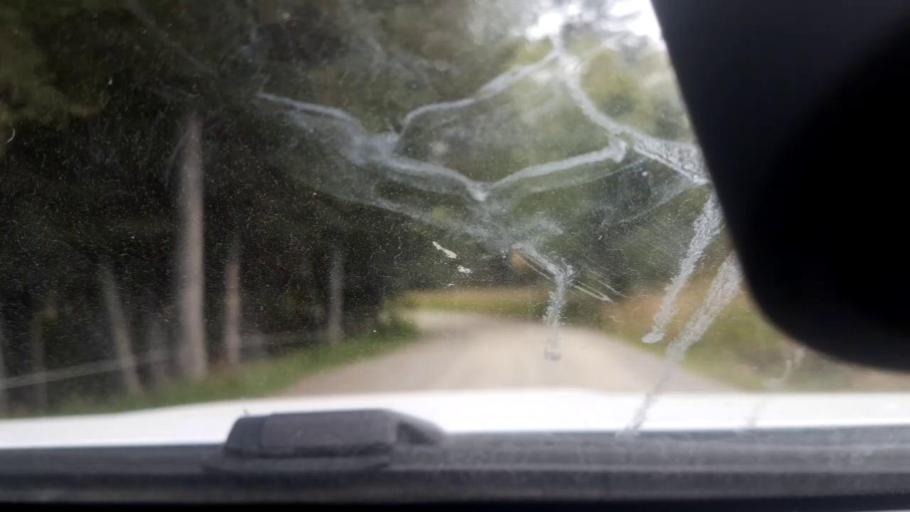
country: NZ
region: Canterbury
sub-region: Timaru District
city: Pleasant Point
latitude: -44.2089
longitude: 171.1787
